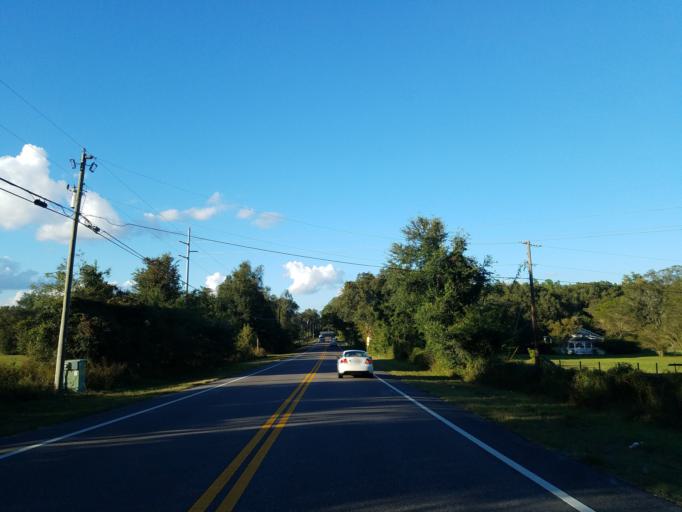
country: US
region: Florida
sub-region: Hernando County
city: Hill 'n Dale
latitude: 28.5063
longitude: -82.3030
